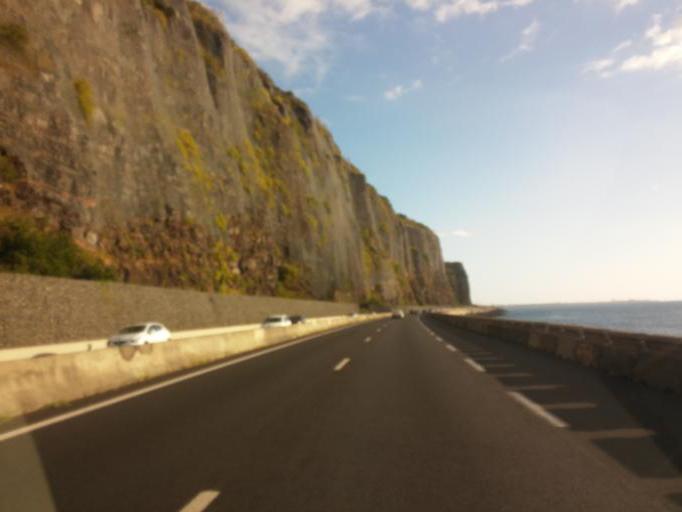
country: RE
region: Reunion
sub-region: Reunion
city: La Possession
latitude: -20.9070
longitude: 55.3617
